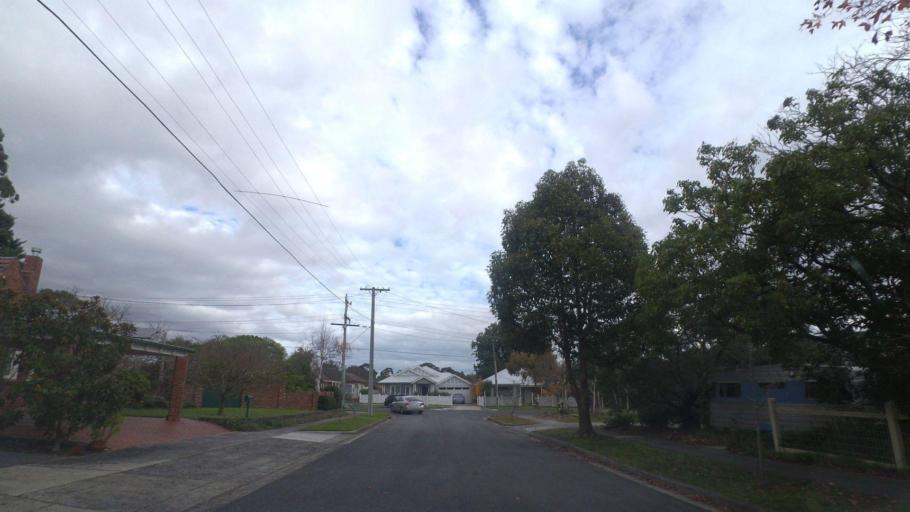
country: AU
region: Victoria
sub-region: Whitehorse
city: Nunawading
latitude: -37.8139
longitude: 145.1652
